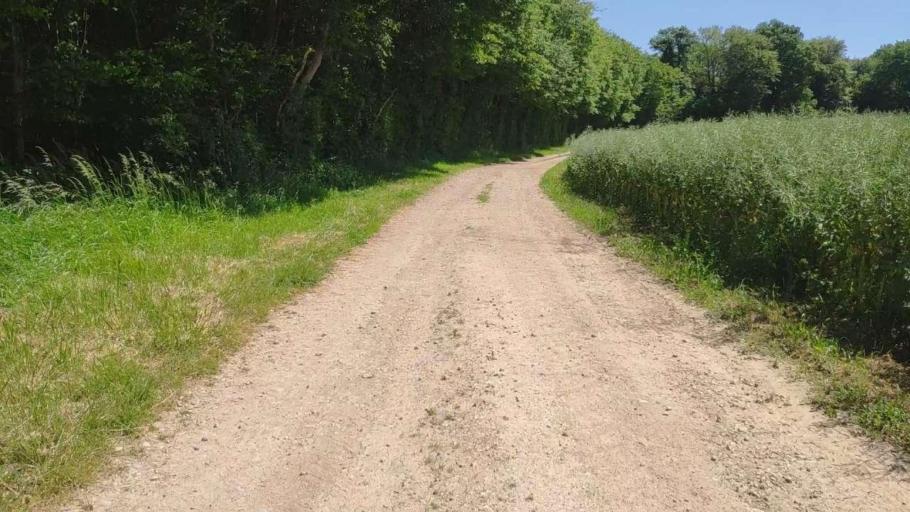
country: FR
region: Franche-Comte
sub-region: Departement du Jura
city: Bletterans
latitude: 46.7722
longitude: 5.3947
